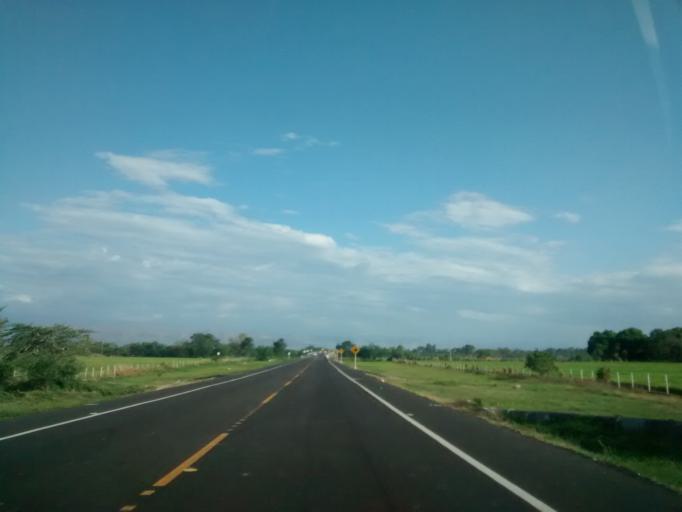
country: CO
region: Tolima
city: Espinal
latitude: 4.1506
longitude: -74.9139
